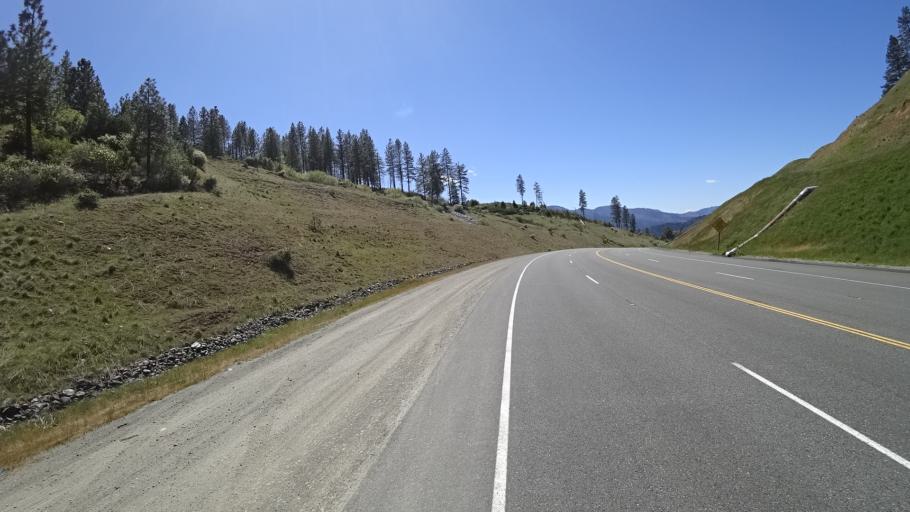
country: US
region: California
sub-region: Trinity County
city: Weaverville
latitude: 40.7379
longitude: -122.9847
